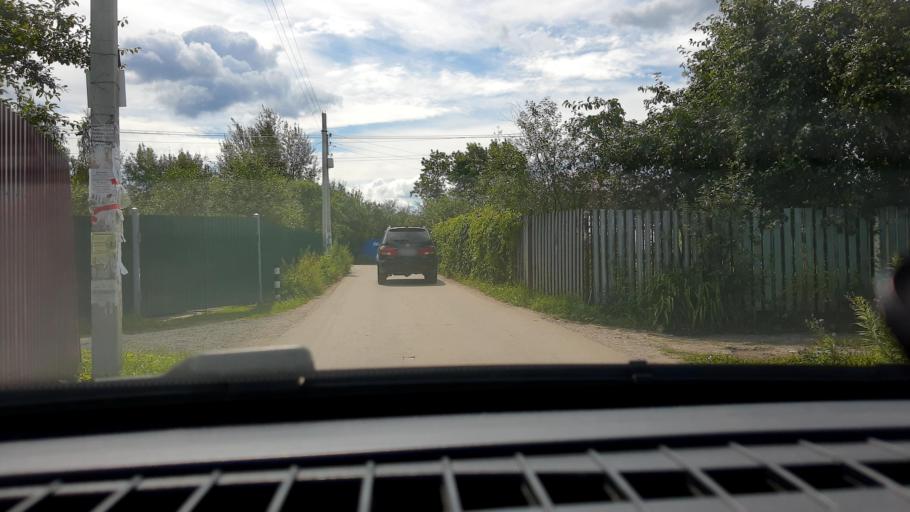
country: RU
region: Nizjnij Novgorod
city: Gorbatovka
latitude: 56.2502
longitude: 43.8130
